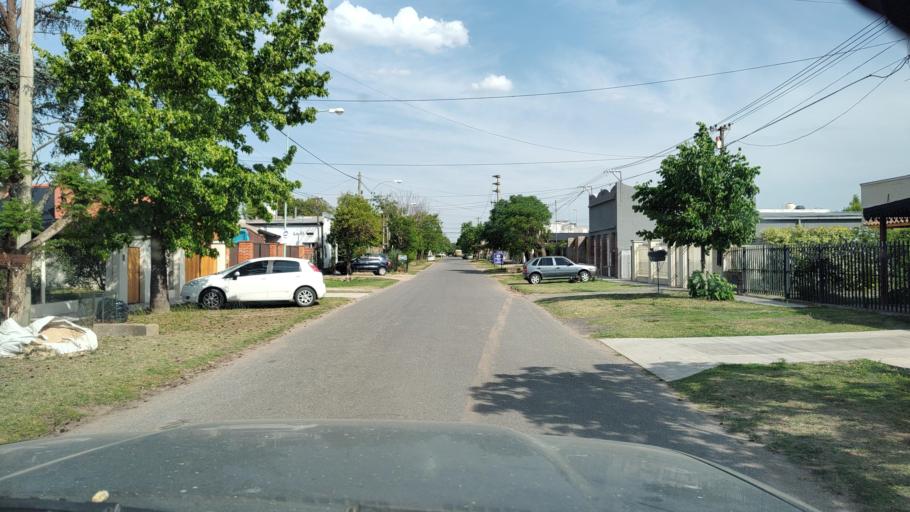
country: AR
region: Buenos Aires
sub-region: Partido de Lujan
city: Lujan
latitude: -34.5966
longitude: -59.1791
